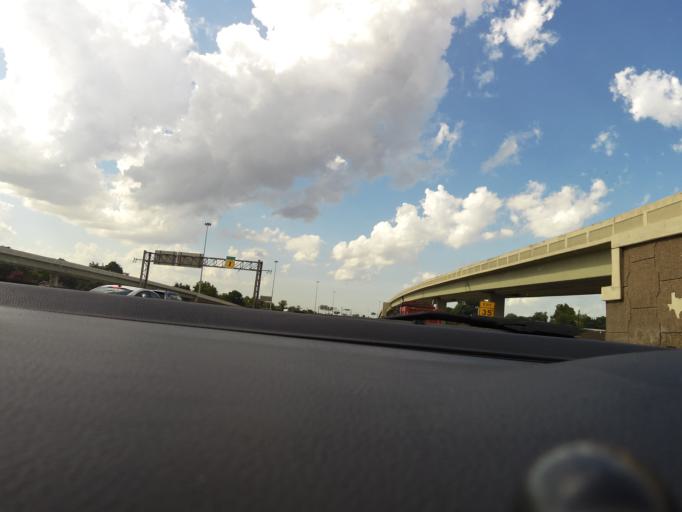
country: US
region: Texas
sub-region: Harris County
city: Aldine
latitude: 29.8537
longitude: -95.3335
